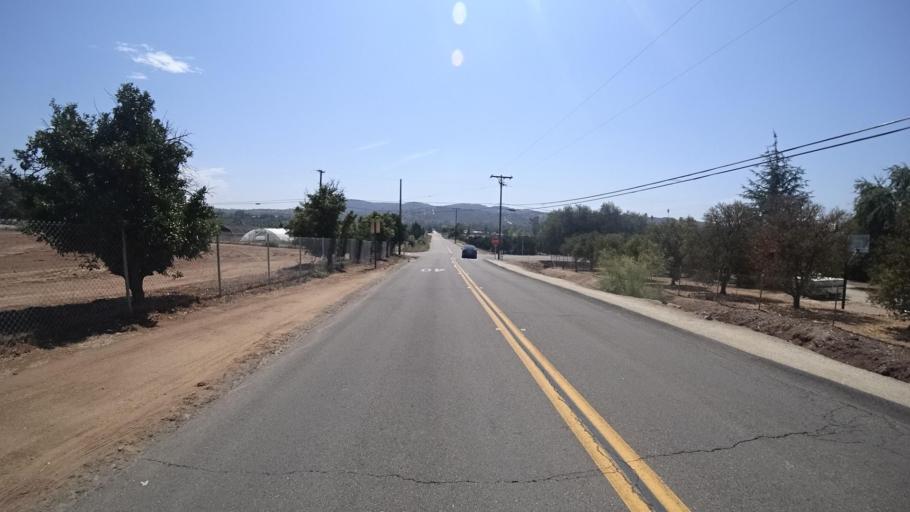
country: US
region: California
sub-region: San Diego County
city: Valley Center
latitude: 33.2362
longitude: -116.9935
